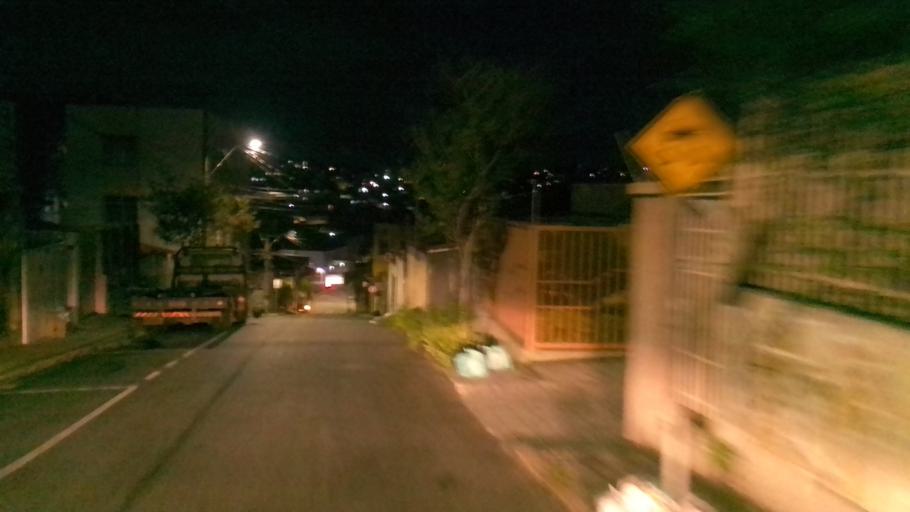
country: BR
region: Minas Gerais
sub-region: Belo Horizonte
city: Belo Horizonte
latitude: -19.9103
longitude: -43.9594
